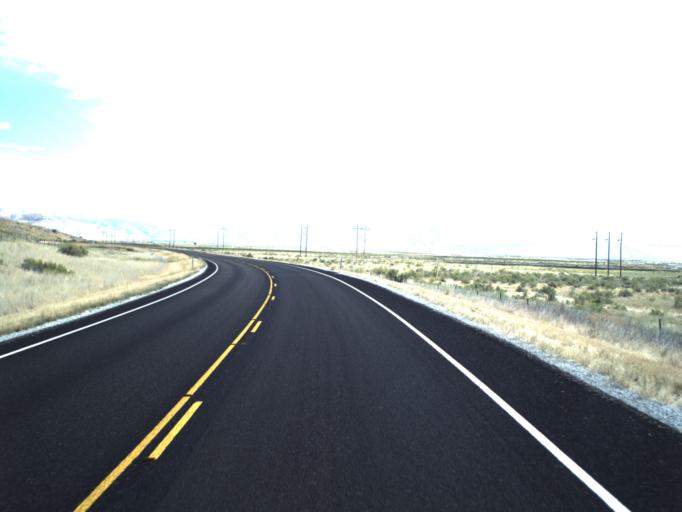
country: US
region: Utah
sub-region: Box Elder County
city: Tremonton
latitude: 41.6152
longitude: -112.3779
